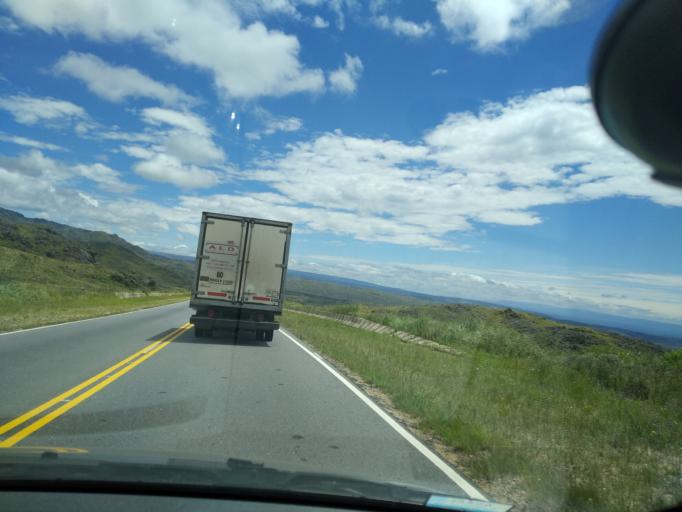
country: AR
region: Cordoba
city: Cuesta Blanca
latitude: -31.6197
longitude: -64.6683
